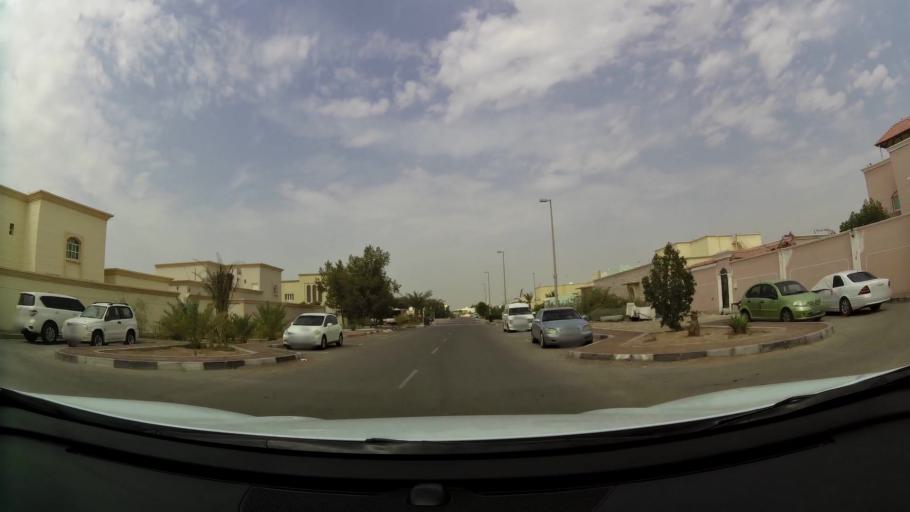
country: AE
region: Abu Dhabi
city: Abu Dhabi
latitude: 24.3107
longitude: 54.6391
